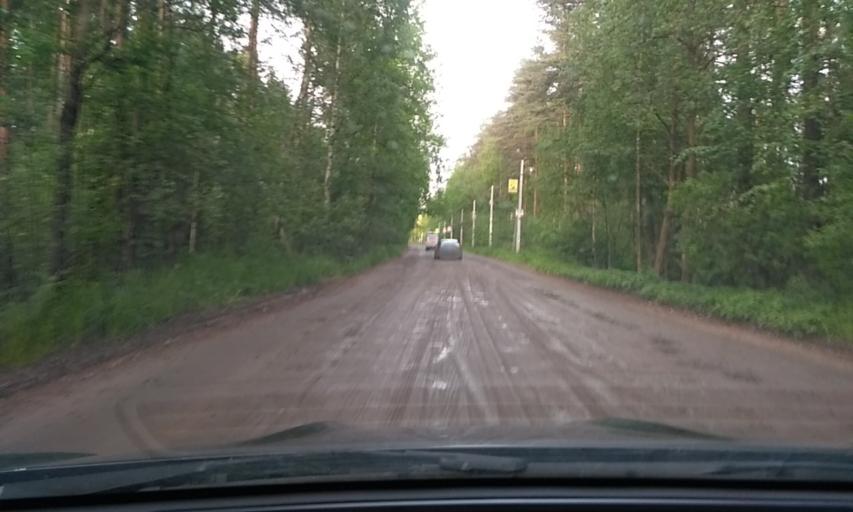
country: RU
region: Leningrad
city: Otradnoye
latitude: 59.7842
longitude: 30.7704
